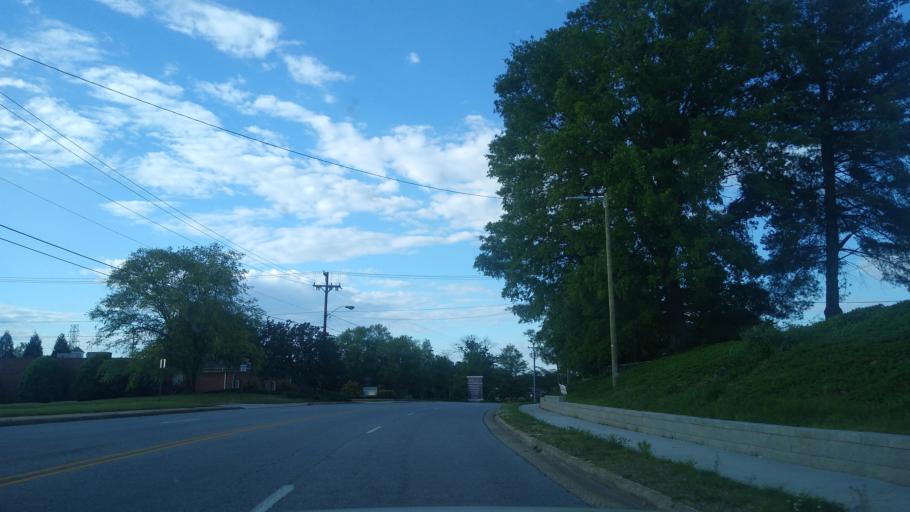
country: US
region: North Carolina
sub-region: Guilford County
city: Greensboro
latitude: 36.0948
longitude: -79.7799
